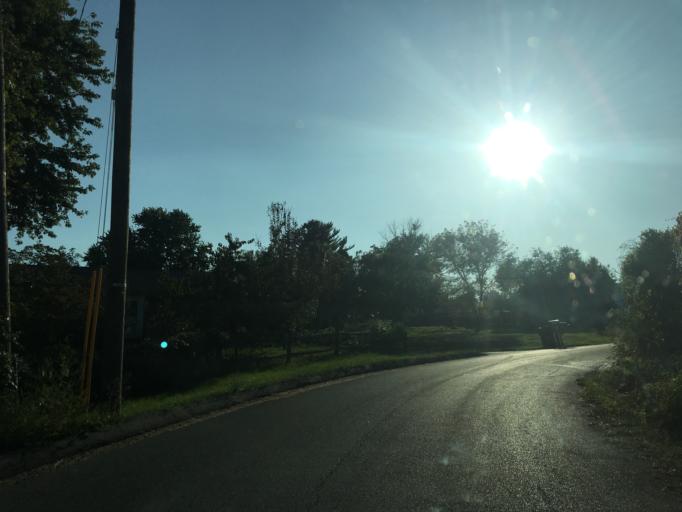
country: US
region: Maryland
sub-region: Howard County
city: Hanover
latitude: 39.1777
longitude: -76.7463
